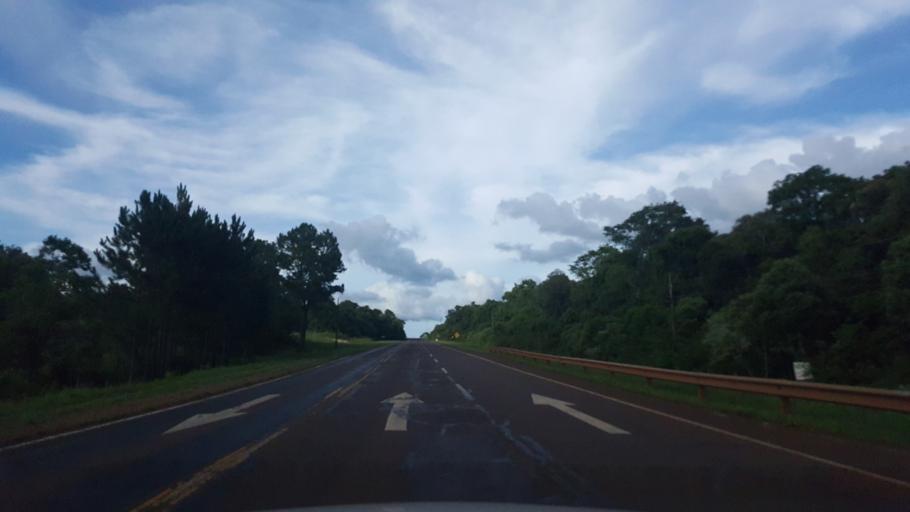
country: AR
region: Misiones
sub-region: Departamento de San Ignacio
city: San Ignacio
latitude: -27.2491
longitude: -55.5222
